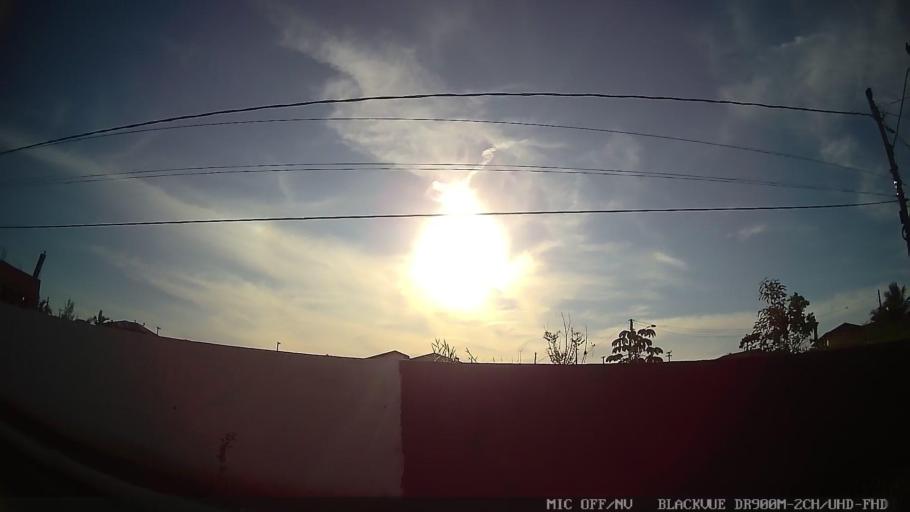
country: BR
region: Sao Paulo
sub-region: Iguape
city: Iguape
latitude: -24.7565
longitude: -47.5675
